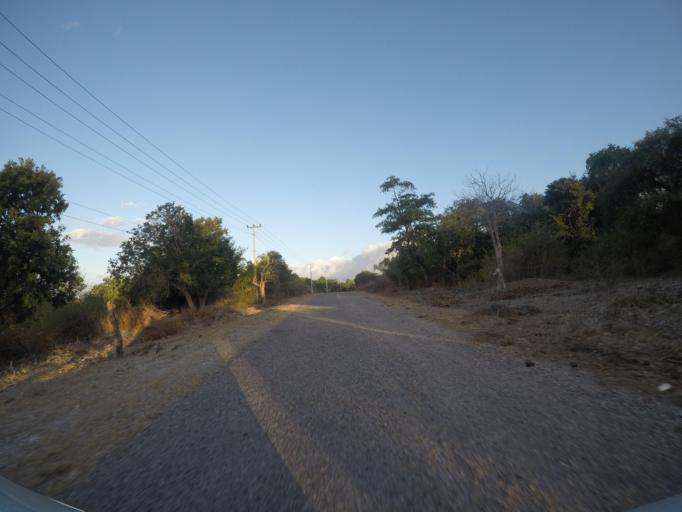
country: TL
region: Lautem
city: Lospalos
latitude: -8.3360
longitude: 127.0119
